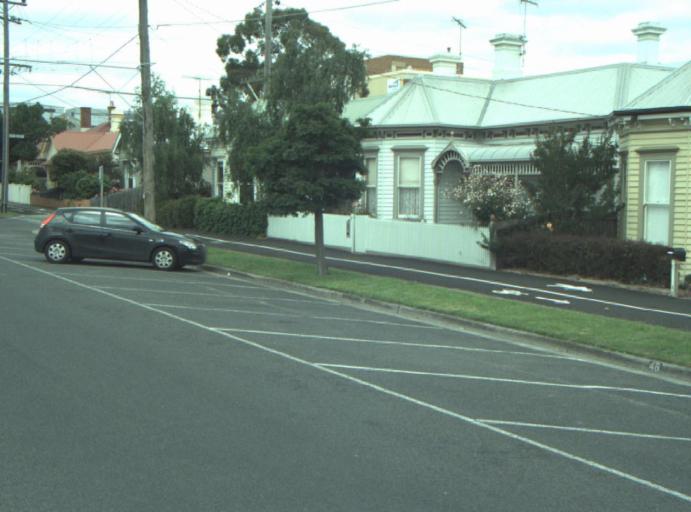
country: AU
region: Victoria
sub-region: Greater Geelong
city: East Geelong
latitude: -38.1500
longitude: 144.3680
